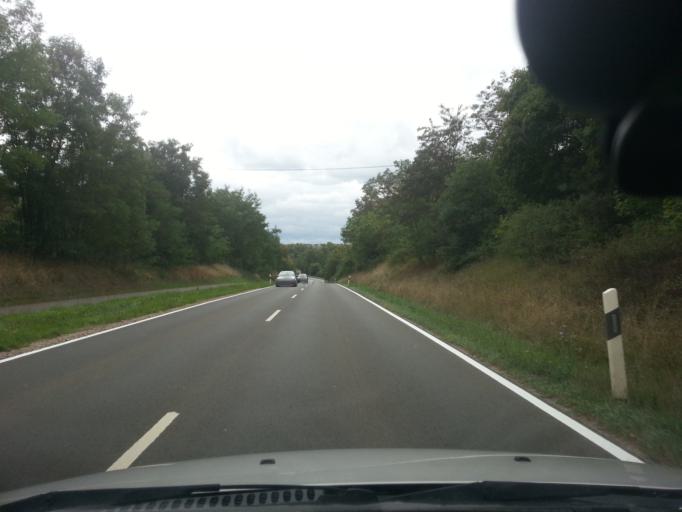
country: DE
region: Rheinland-Pfalz
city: Eisenberg
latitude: 49.5484
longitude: 8.0728
